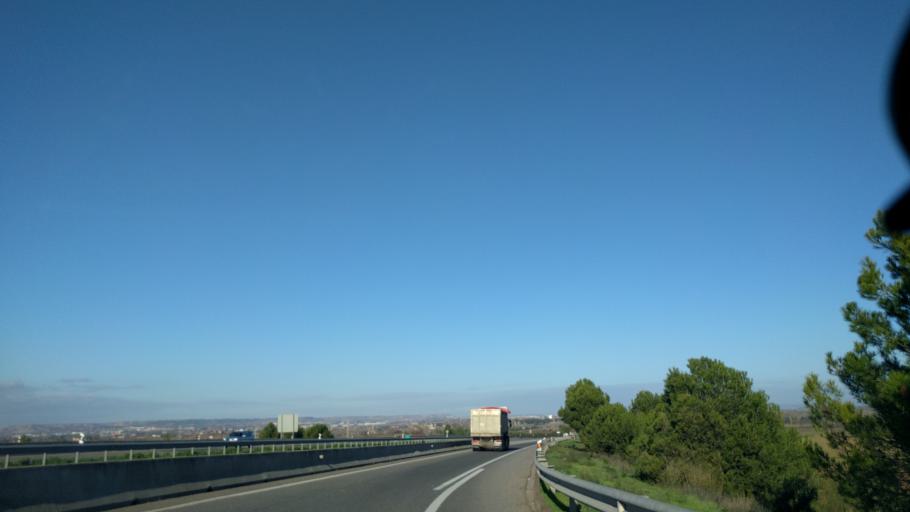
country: ES
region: Catalonia
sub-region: Provincia de Lleida
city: Alcoletge
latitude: 41.6430
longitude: 0.6747
